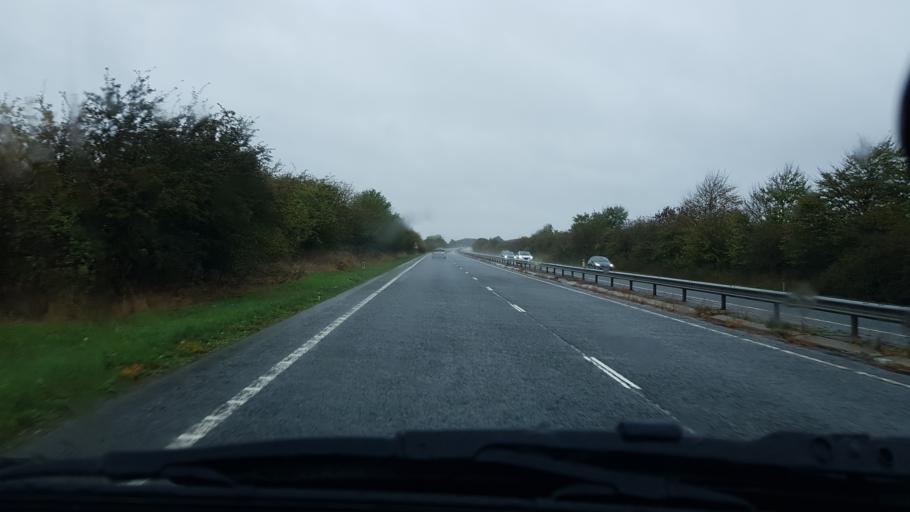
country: GB
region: England
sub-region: Oxfordshire
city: Carterton
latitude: 51.7846
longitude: -1.5633
